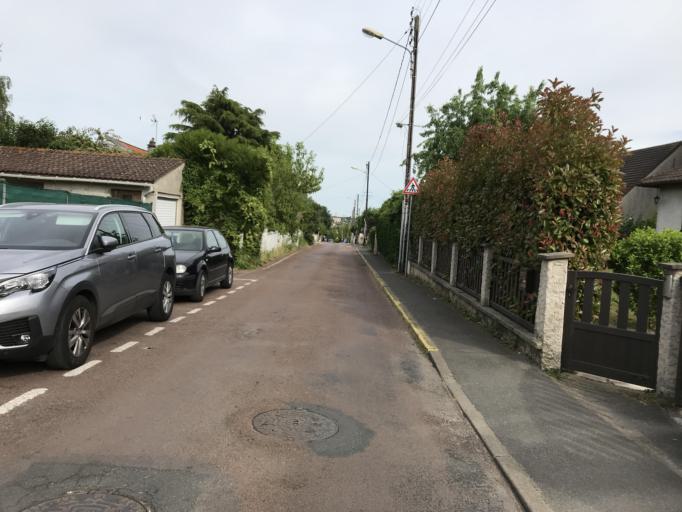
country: FR
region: Ile-de-France
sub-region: Departement de l'Essonne
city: Longpont-sur-Orge
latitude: 48.6335
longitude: 2.2851
